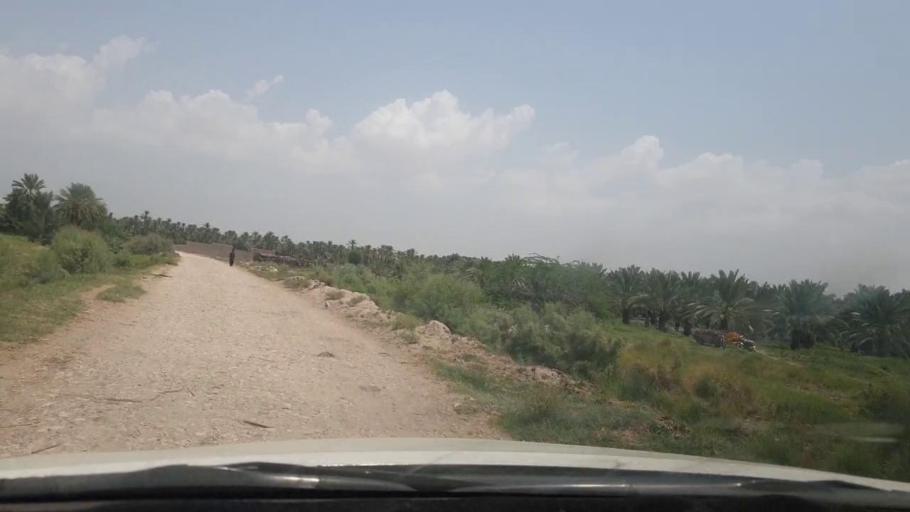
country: PK
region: Sindh
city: Khairpur
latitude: 27.5476
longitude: 68.8238
